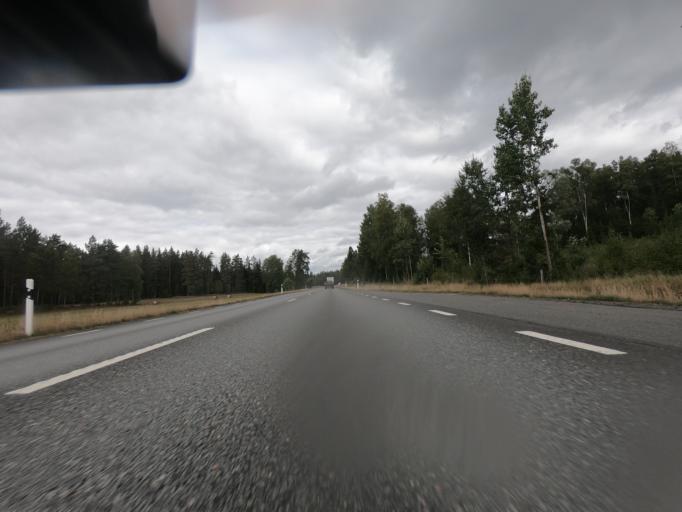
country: SE
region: Joenkoeping
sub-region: Vaggeryds Kommun
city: Vaggeryd
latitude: 57.4495
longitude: 14.3183
